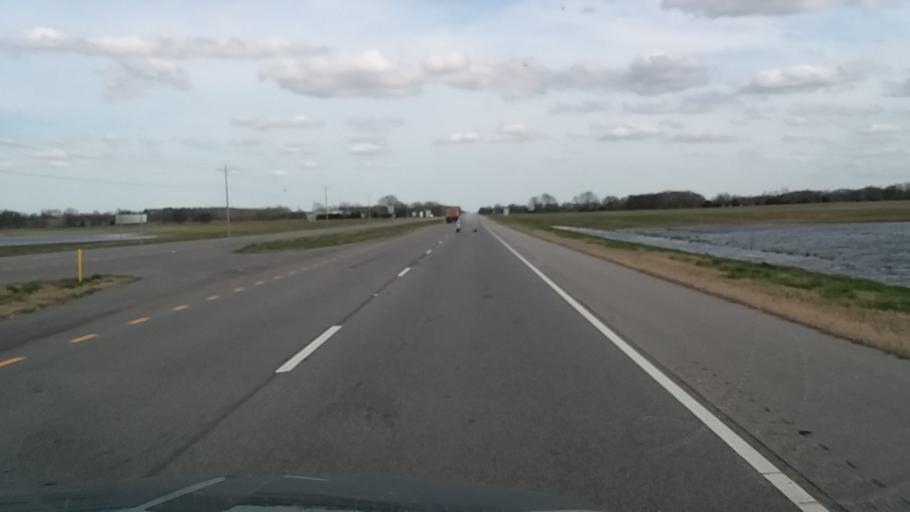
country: US
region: Alabama
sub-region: Lawrence County
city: Town Creek
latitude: 34.6838
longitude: -87.5271
